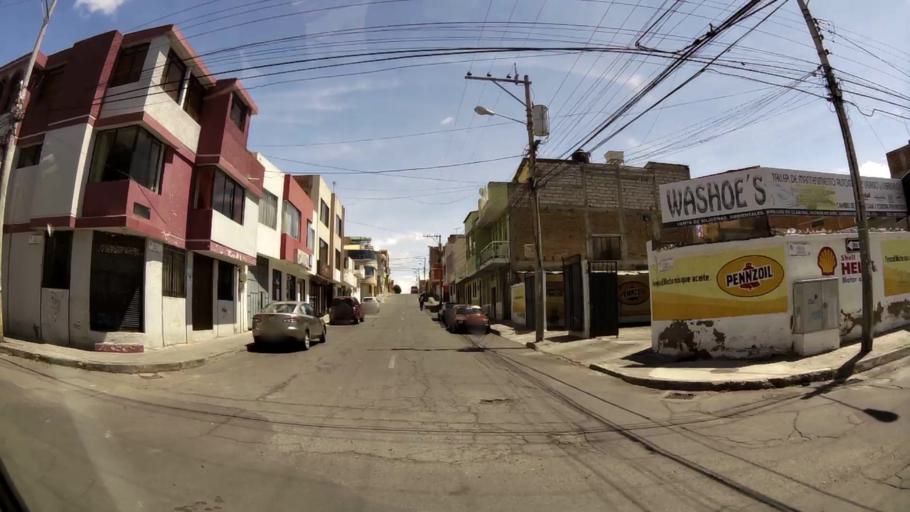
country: EC
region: Chimborazo
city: Riobamba
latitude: -1.6608
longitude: -78.6600
